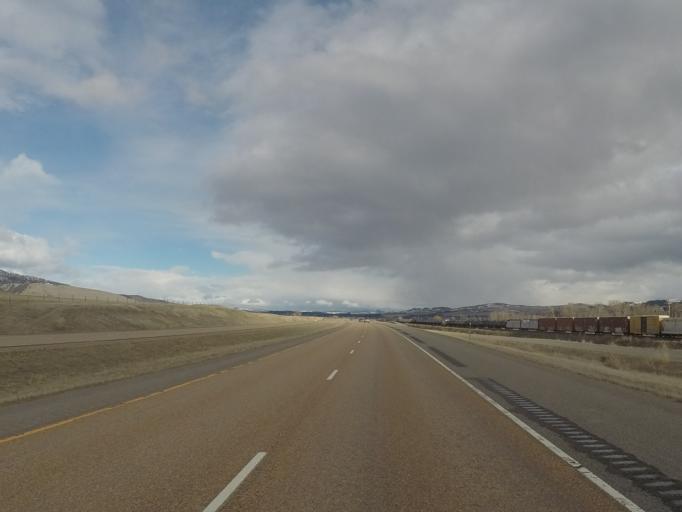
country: US
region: Montana
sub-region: Granite County
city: Philipsburg
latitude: 46.6199
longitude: -113.0603
